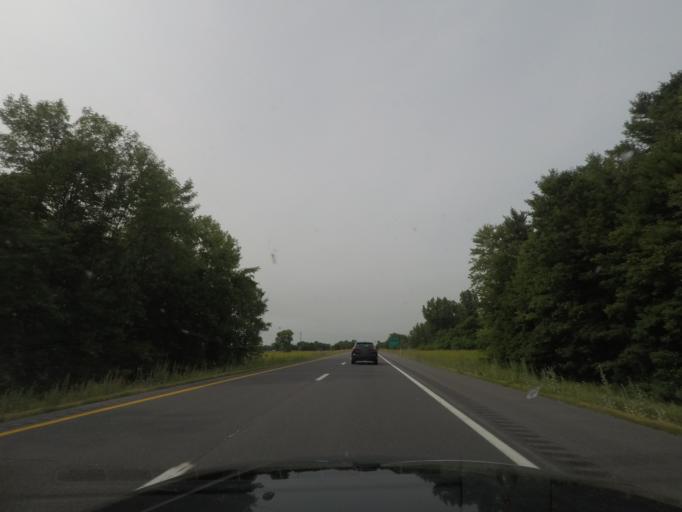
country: US
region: New York
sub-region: Clinton County
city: Cumberland Head
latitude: 44.7614
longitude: -73.4305
